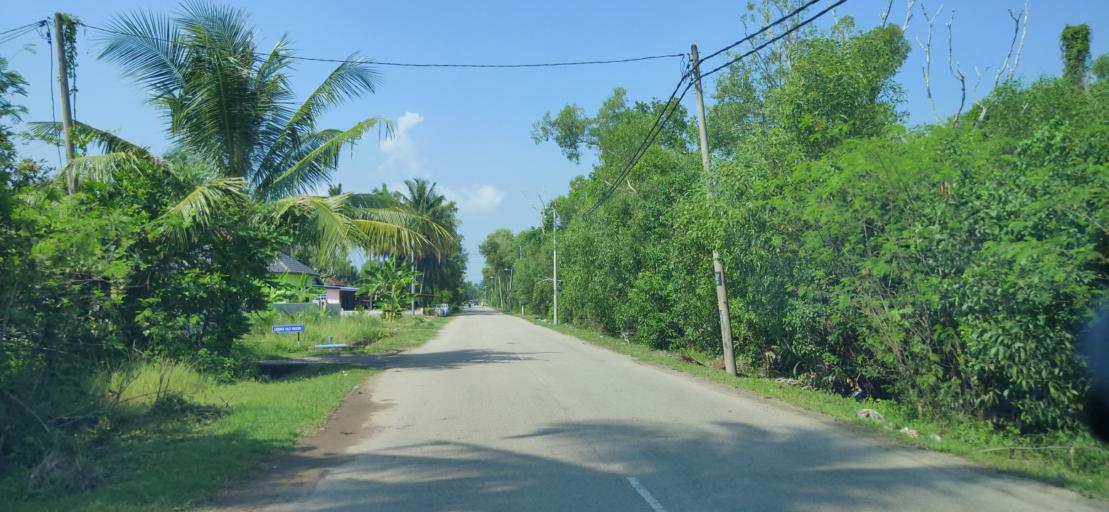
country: MY
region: Kedah
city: Sungai Petani
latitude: 5.6662
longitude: 100.4609
